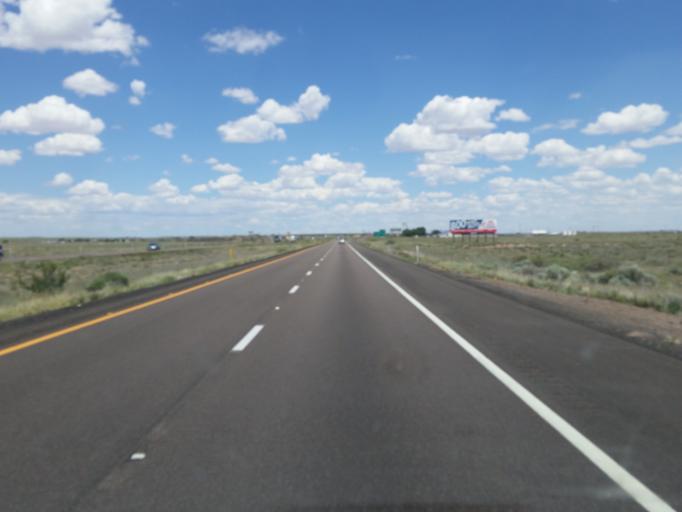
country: US
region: Arizona
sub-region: Navajo County
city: Holbrook
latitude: 34.9784
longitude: -110.0668
